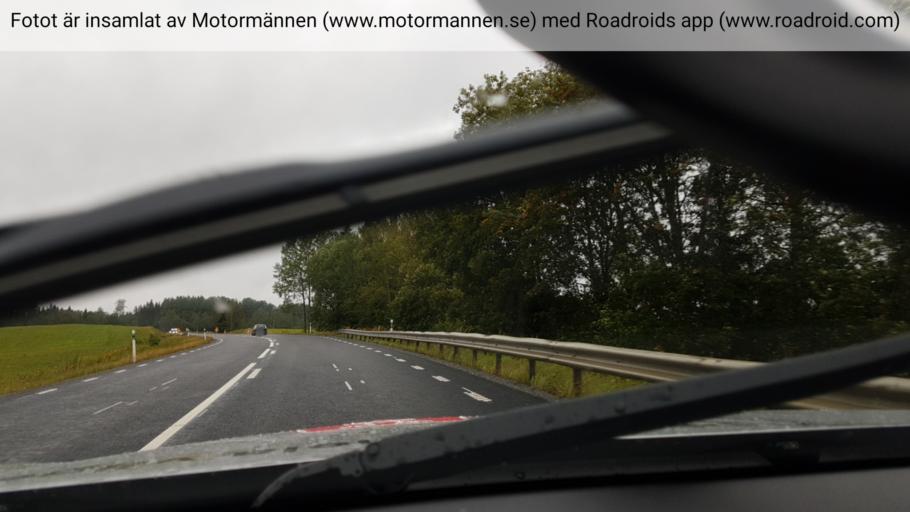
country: SE
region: Vaestra Goetaland
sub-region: Dals-Ed Kommun
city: Ed
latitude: 58.9029
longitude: 11.9865
